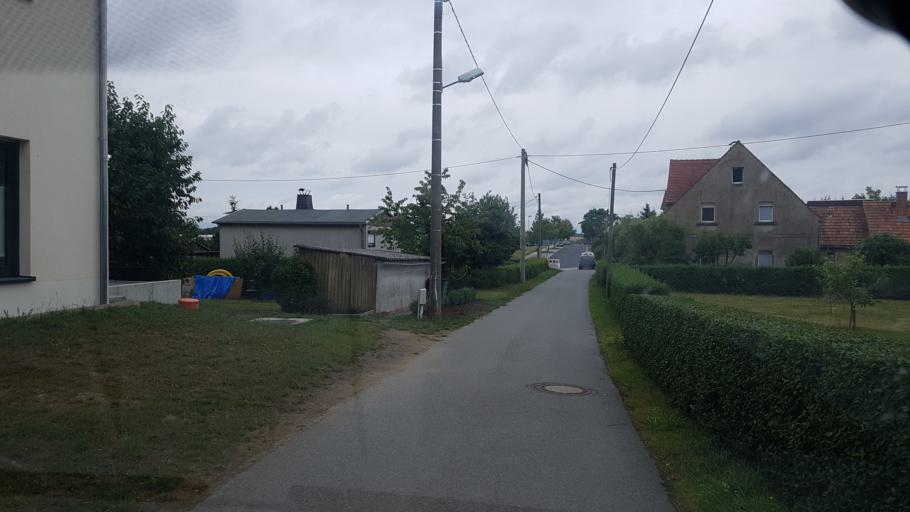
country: DE
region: Saxony
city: Ohorn
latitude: 51.1577
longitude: 14.0437
